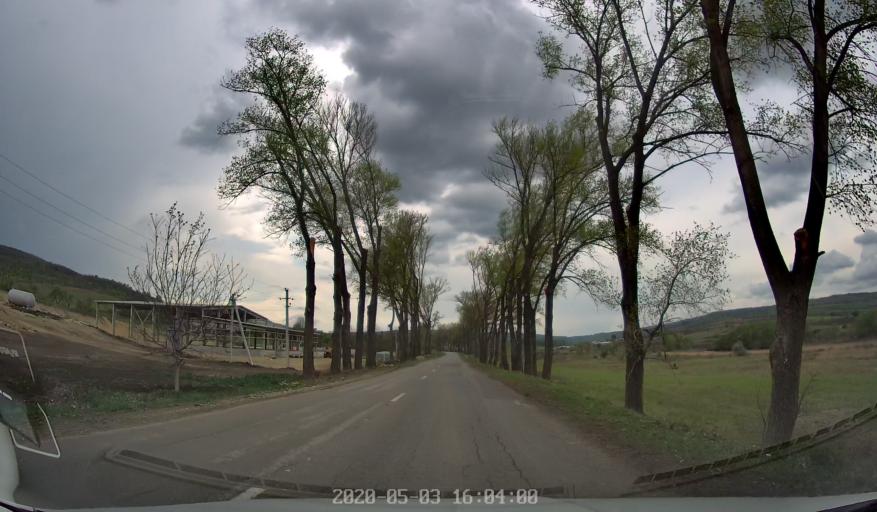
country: MD
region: Stinga Nistrului
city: Bucovat
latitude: 47.1838
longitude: 28.3735
